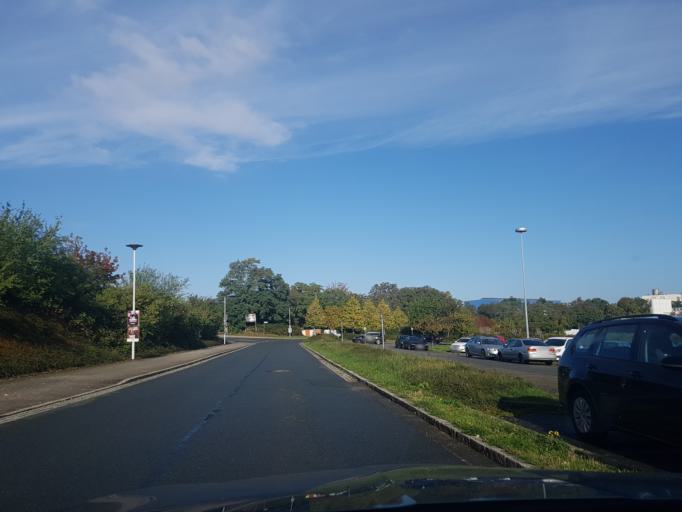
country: DE
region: Saxony
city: Riesa
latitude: 51.2955
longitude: 13.2937
